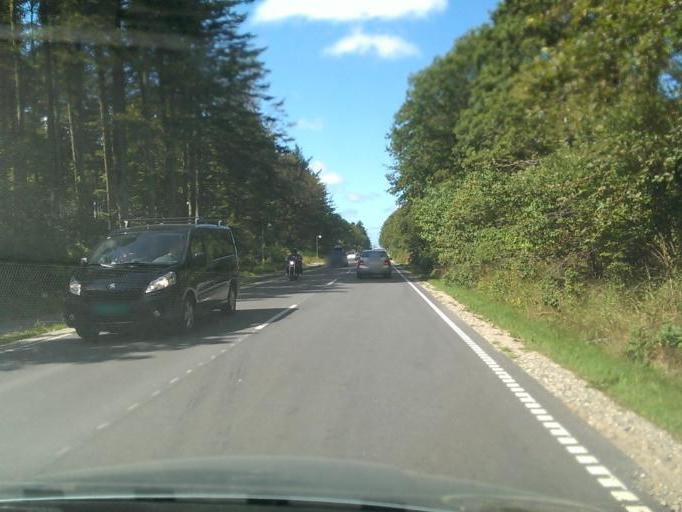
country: DK
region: North Denmark
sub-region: Jammerbugt Kommune
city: Pandrup
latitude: 57.2492
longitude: 9.6102
